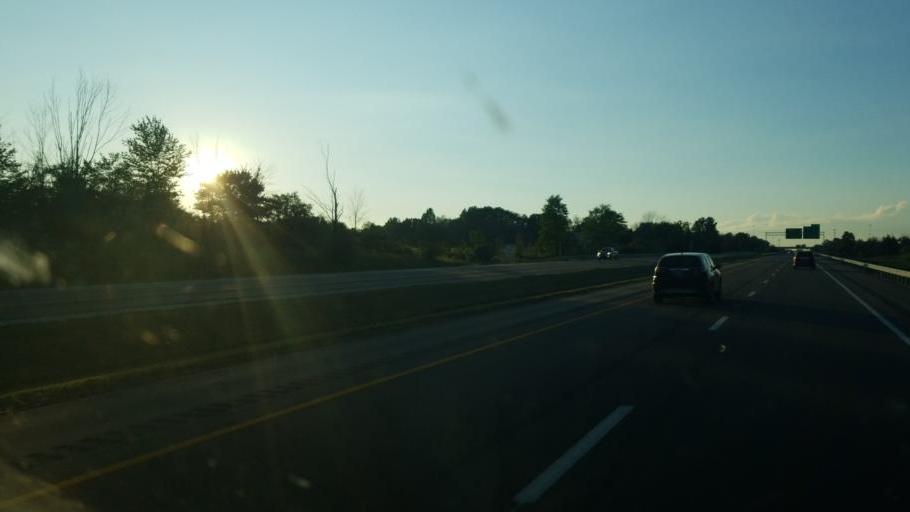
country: US
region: Ohio
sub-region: Mahoning County
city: Austintown
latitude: 41.0970
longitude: -80.8273
